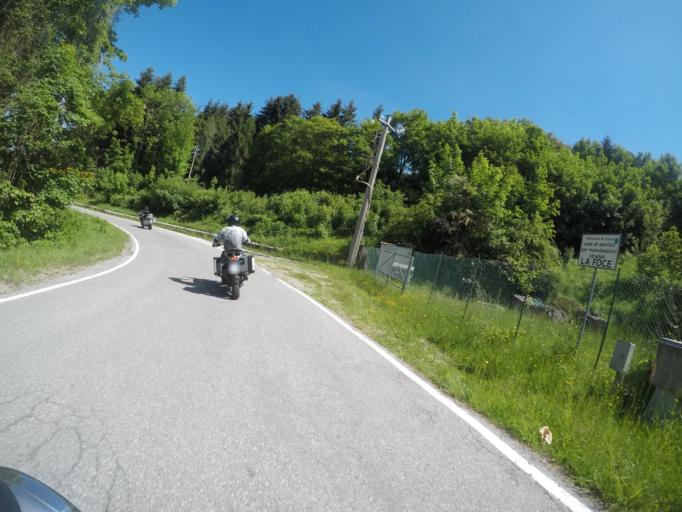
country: IT
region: Tuscany
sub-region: Provincia di Lucca
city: Careggine
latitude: 44.1035
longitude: 10.3337
